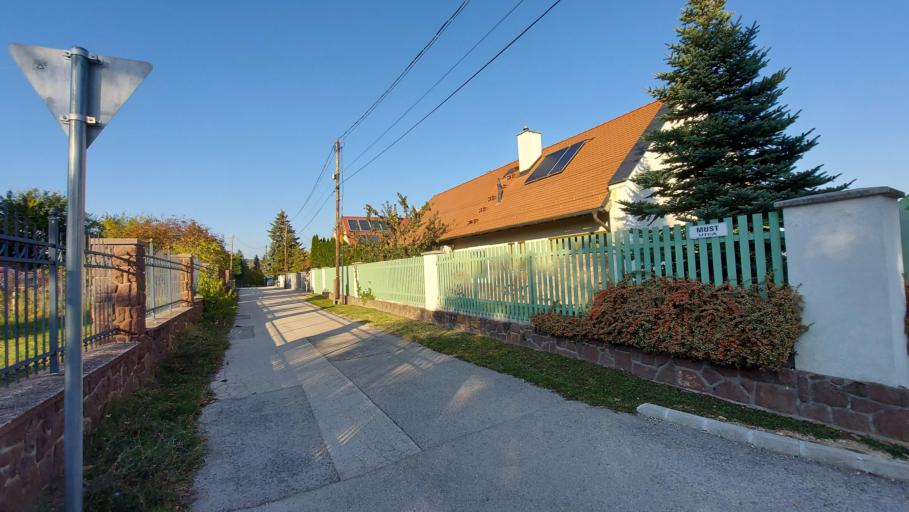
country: HU
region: Veszprem
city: Balatonalmadi
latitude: 47.0361
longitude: 18.0000
